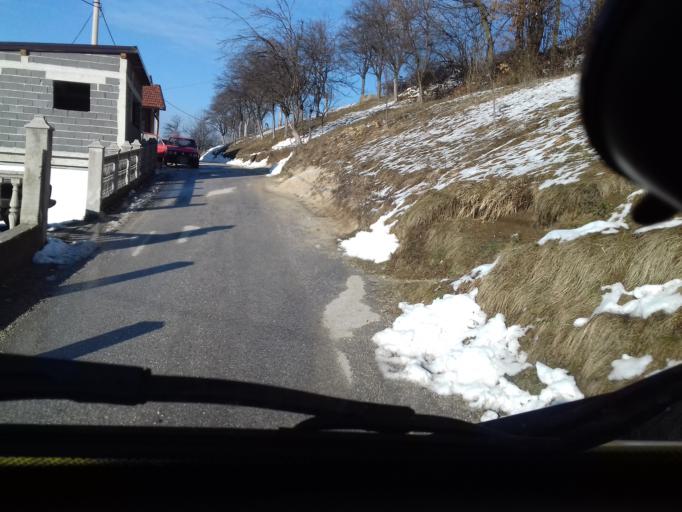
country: BA
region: Federation of Bosnia and Herzegovina
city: Zenica
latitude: 44.1833
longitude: 17.8864
